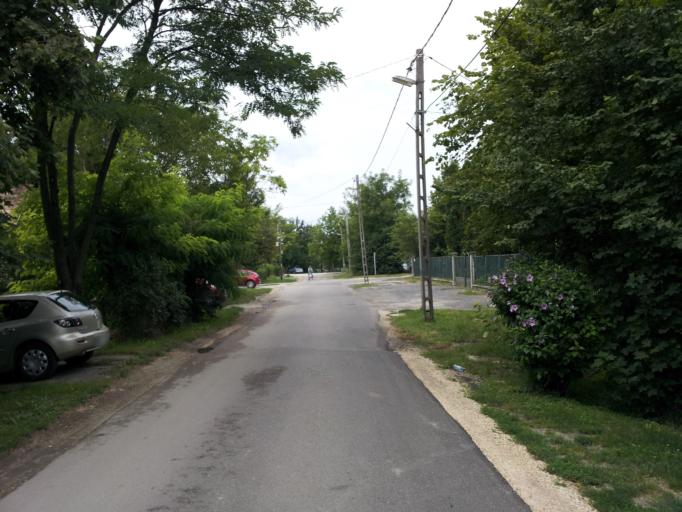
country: HU
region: Pest
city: Rackeve
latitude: 47.1949
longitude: 18.9596
